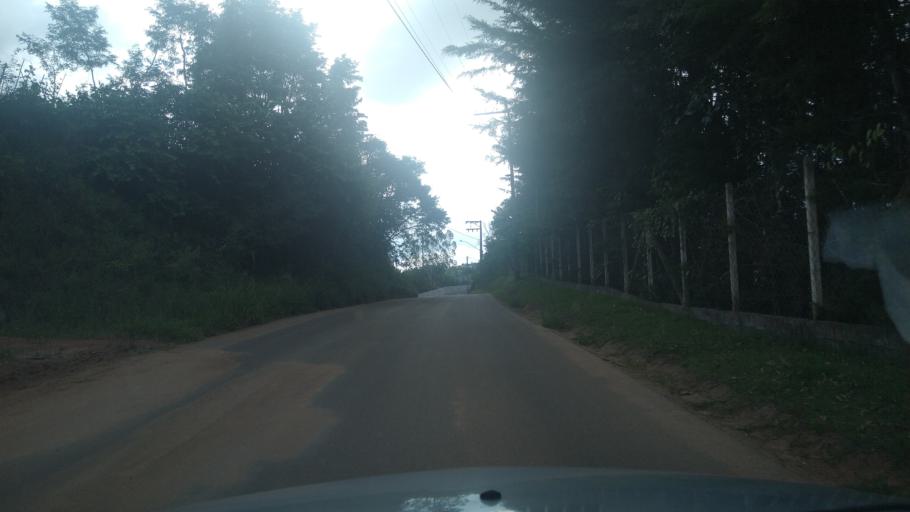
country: BR
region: Minas Gerais
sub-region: Extrema
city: Extrema
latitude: -22.7213
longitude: -46.3429
